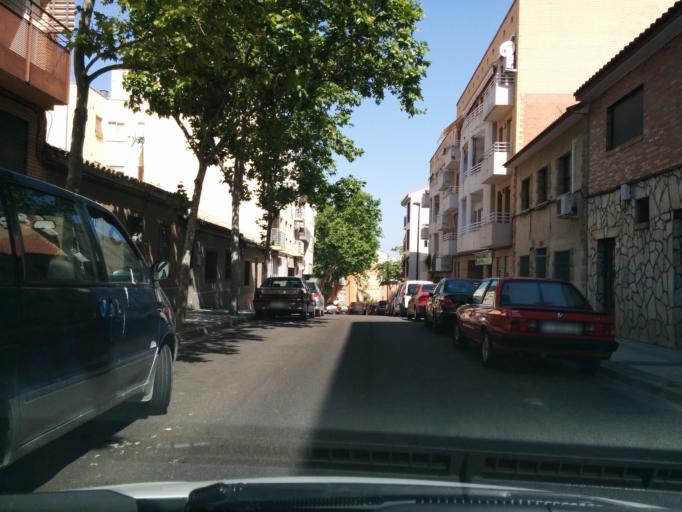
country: ES
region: Aragon
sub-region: Provincia de Zaragoza
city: Zaragoza
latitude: 41.6283
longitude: -0.8759
